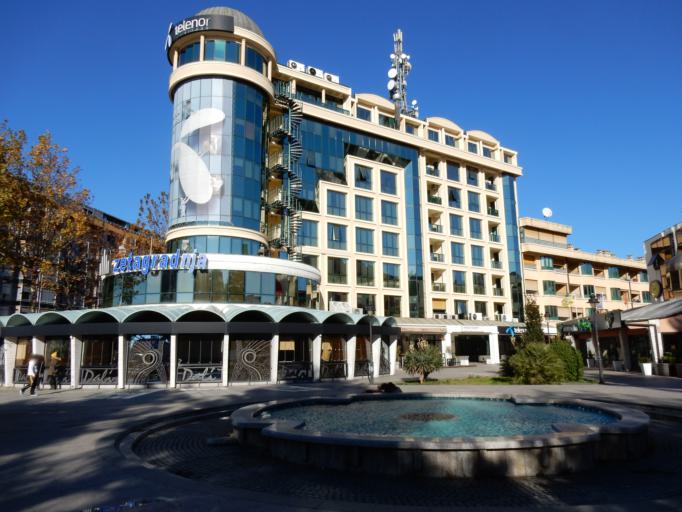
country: ME
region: Podgorica
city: Podgorica
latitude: 42.4414
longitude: 19.2454
